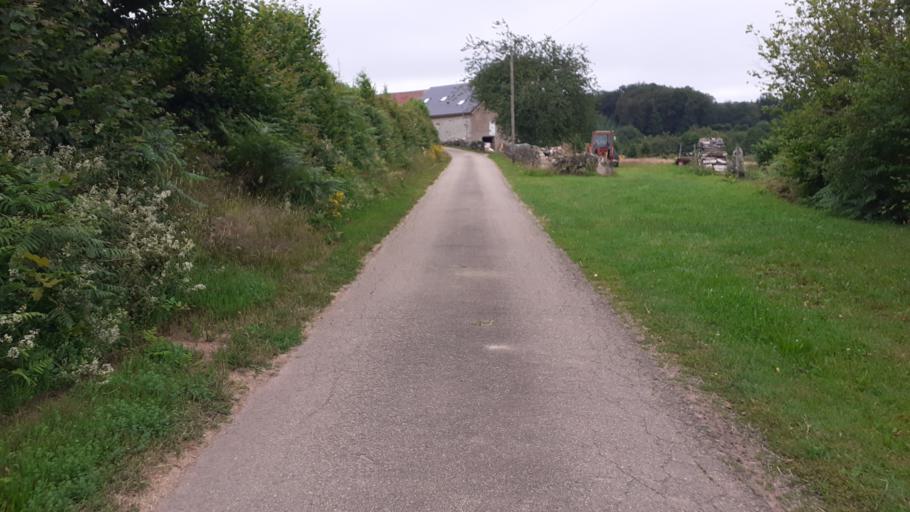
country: FR
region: Bourgogne
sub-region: Departement de la Cote-d'Or
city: Saulieu
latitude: 47.2693
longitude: 4.1383
